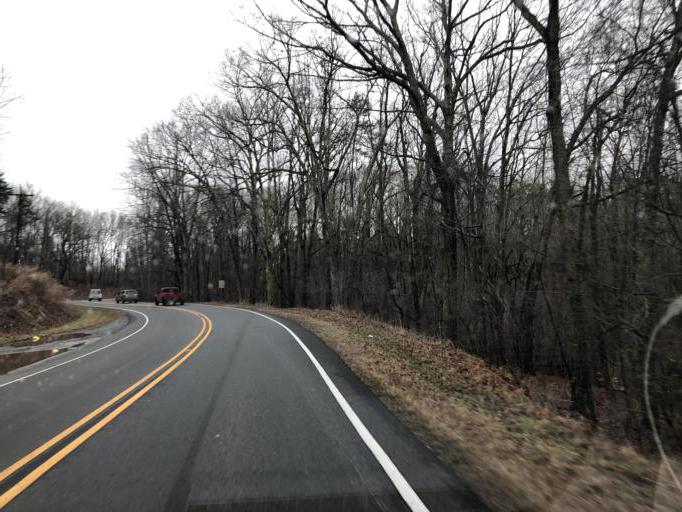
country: US
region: North Carolina
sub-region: Gaston County
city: Ranlo
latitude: 35.2978
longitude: -81.1194
